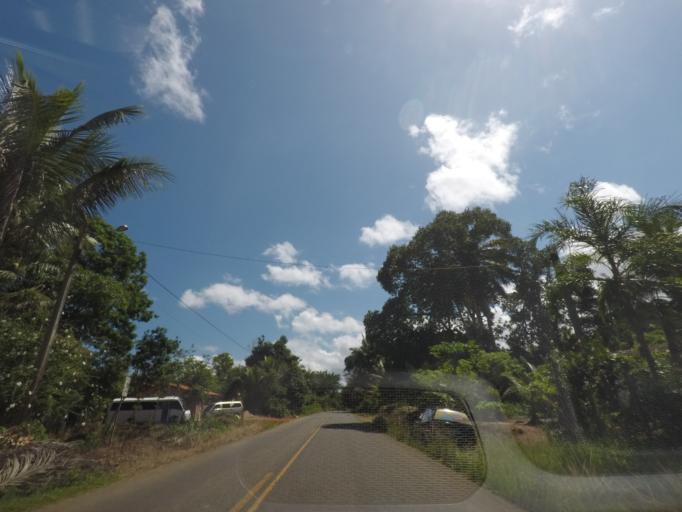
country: BR
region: Bahia
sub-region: Taperoa
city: Taperoa
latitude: -13.4911
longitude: -39.0928
